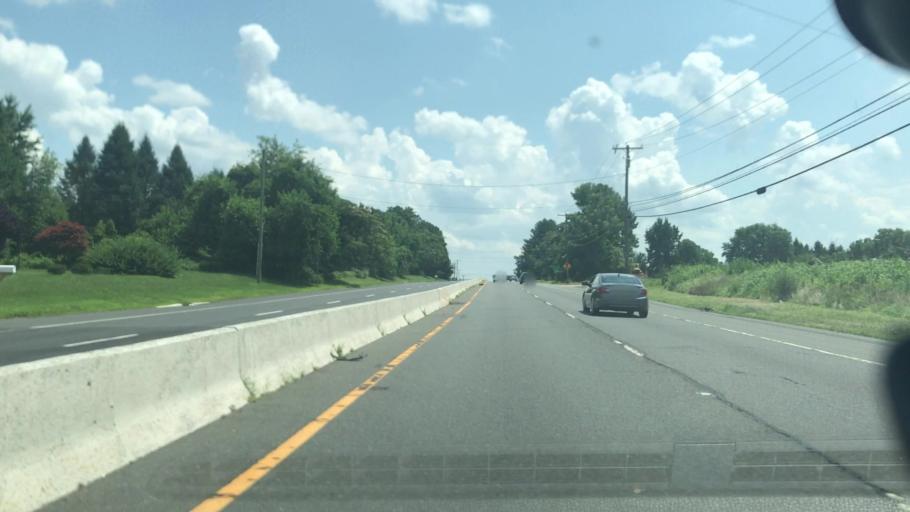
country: US
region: New Jersey
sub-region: Hunterdon County
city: Flemington
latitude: 40.4544
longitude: -74.8596
